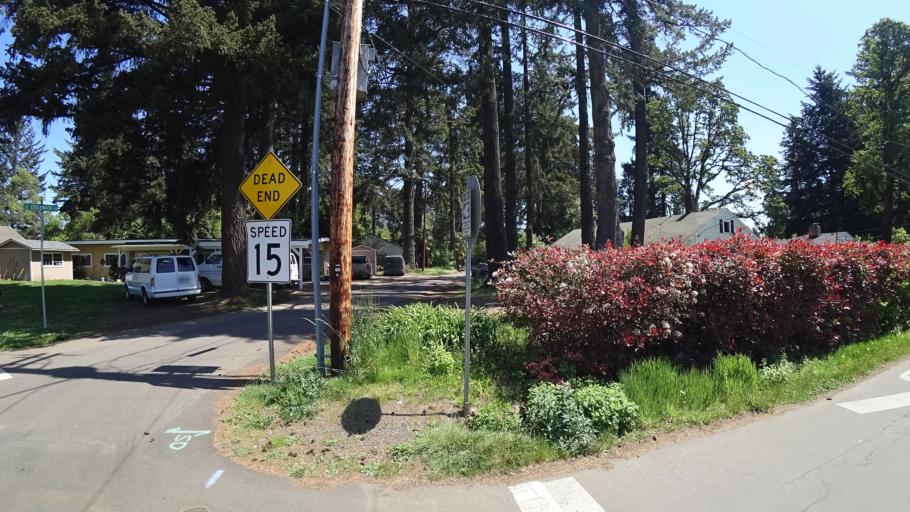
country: US
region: Oregon
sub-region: Washington County
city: Hillsboro
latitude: 45.5134
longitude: -122.9792
